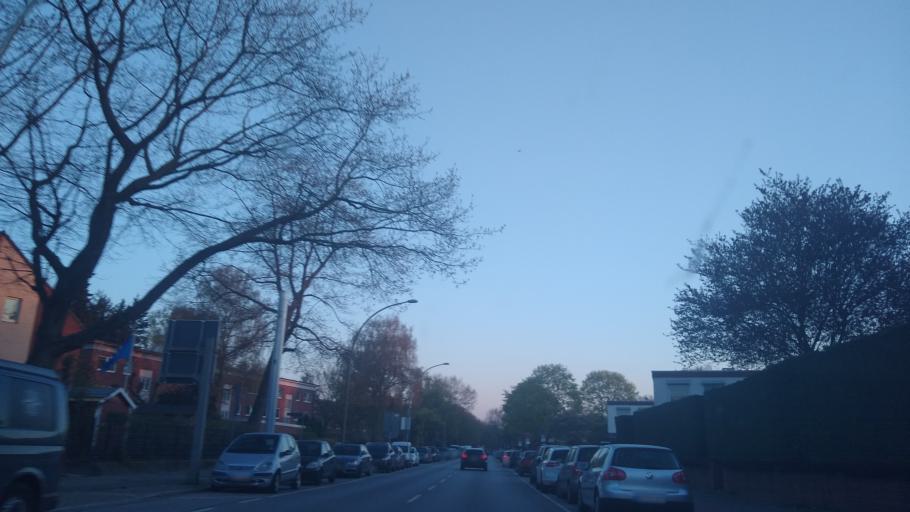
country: DE
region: Schleswig-Holstein
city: Bonningstedt
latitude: 53.6384
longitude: 9.9190
